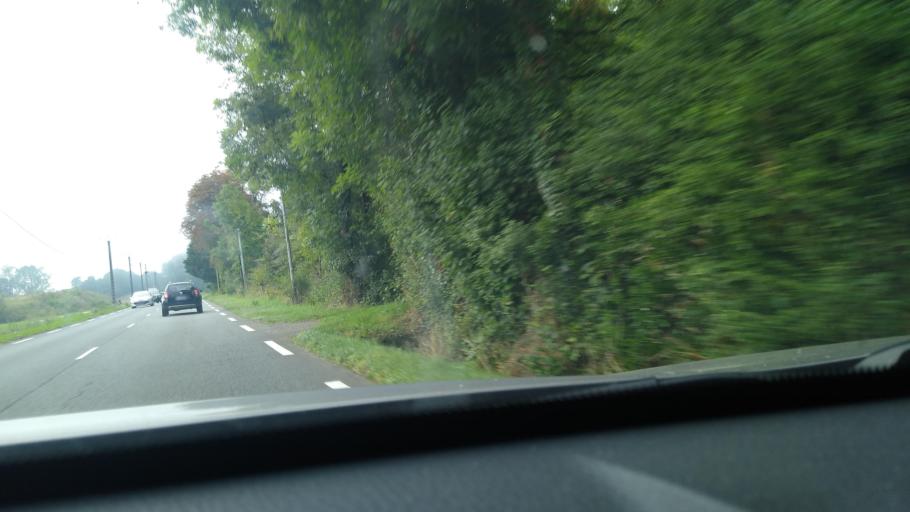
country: FR
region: Midi-Pyrenees
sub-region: Departement de la Haute-Garonne
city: Salies-du-Salat
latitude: 43.0757
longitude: 0.9608
